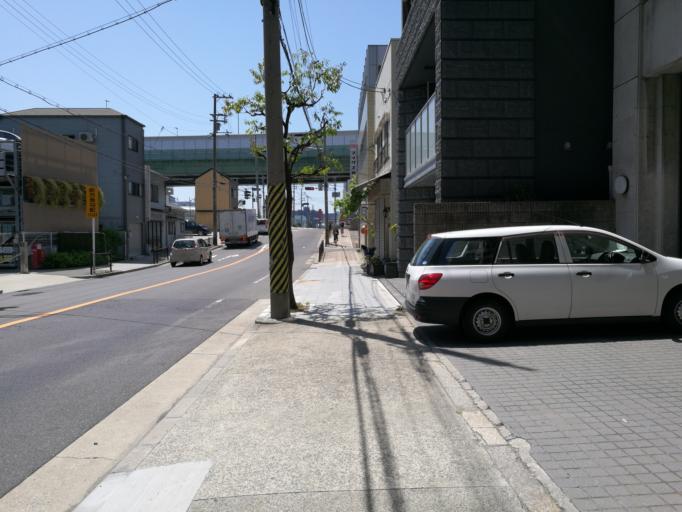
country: JP
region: Osaka
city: Osaka-shi
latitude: 34.6879
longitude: 135.4828
